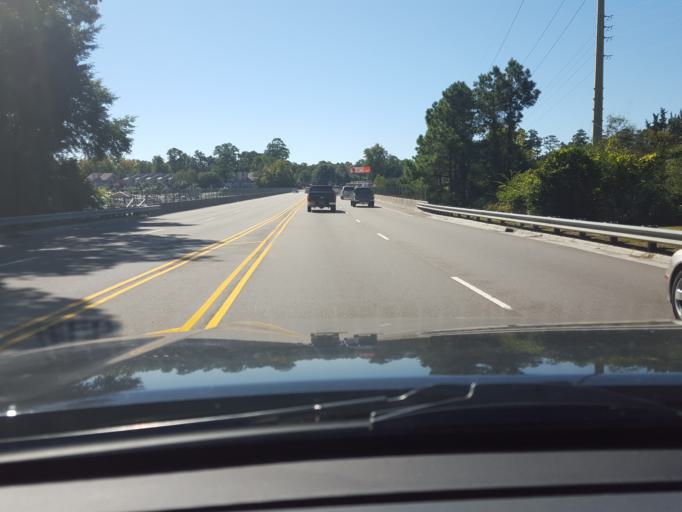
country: US
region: North Carolina
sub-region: New Hanover County
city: Seagate
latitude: 34.2171
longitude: -77.8337
